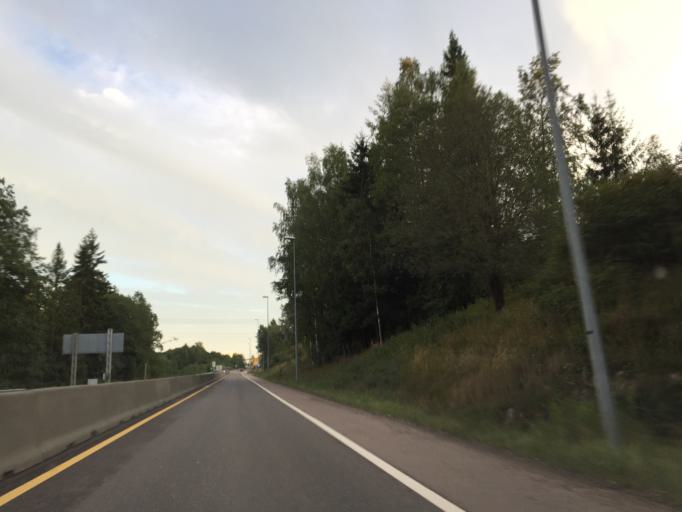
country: NO
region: Akershus
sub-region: Ski
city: Ski
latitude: 59.7323
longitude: 10.7838
